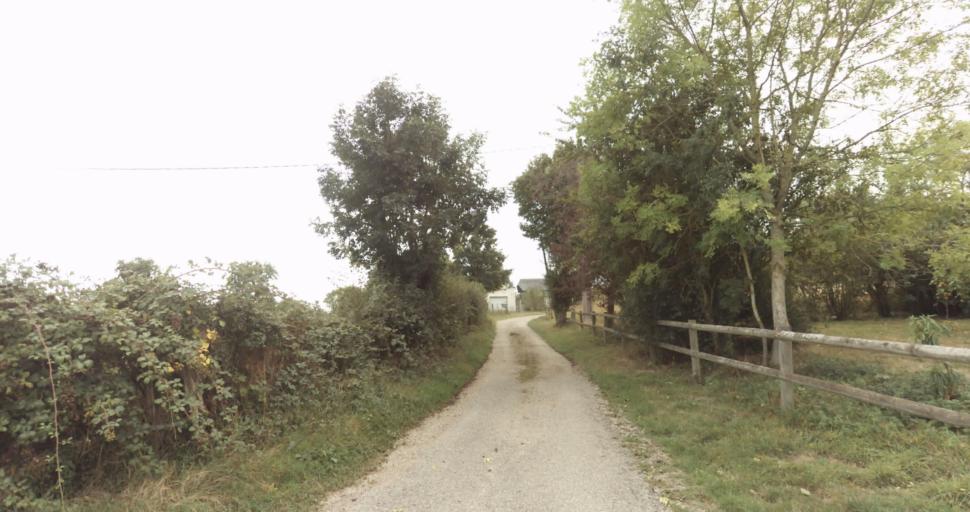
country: FR
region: Lower Normandy
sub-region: Departement de l'Orne
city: Gace
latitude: 48.8678
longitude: 0.2630
